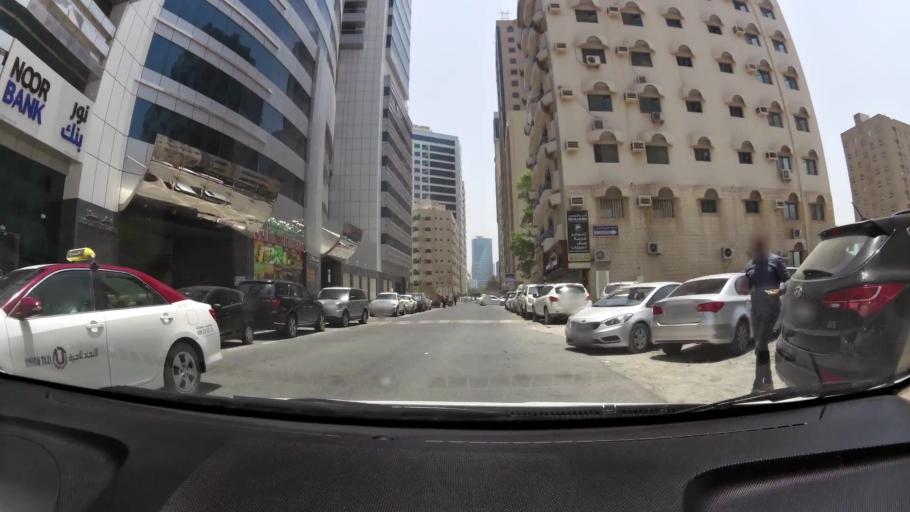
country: AE
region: Ash Shariqah
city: Sharjah
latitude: 25.3368
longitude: 55.3755
